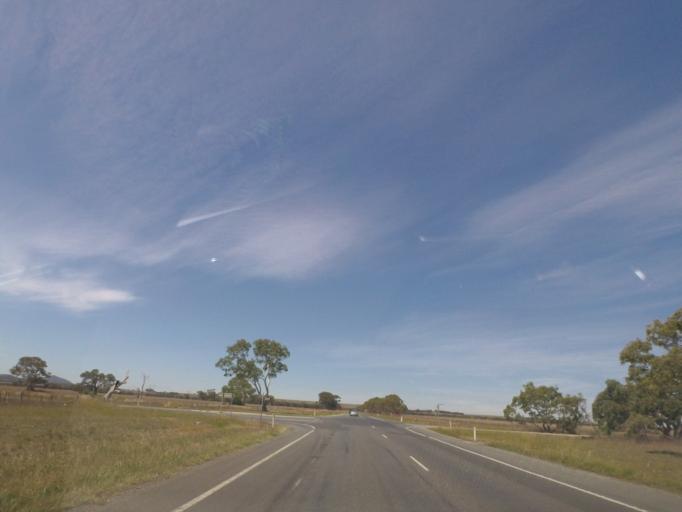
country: AU
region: Victoria
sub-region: Wyndham
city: Little River
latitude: -37.8732
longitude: 144.3820
